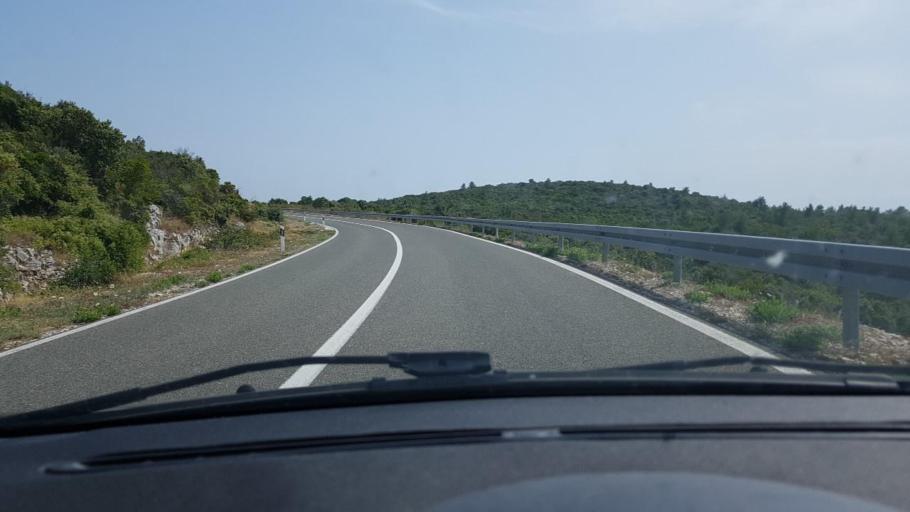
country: HR
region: Dubrovacko-Neretvanska
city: Smokvica
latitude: 42.9508
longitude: 16.9418
